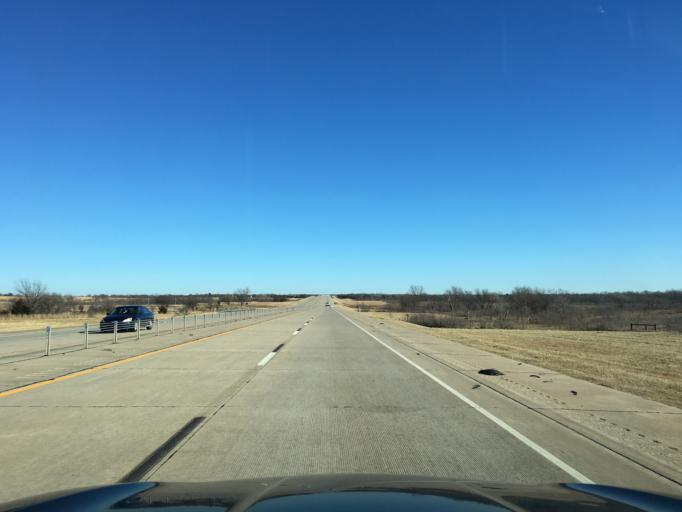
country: US
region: Oklahoma
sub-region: Payne County
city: Yale
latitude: 36.2249
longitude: -96.6949
